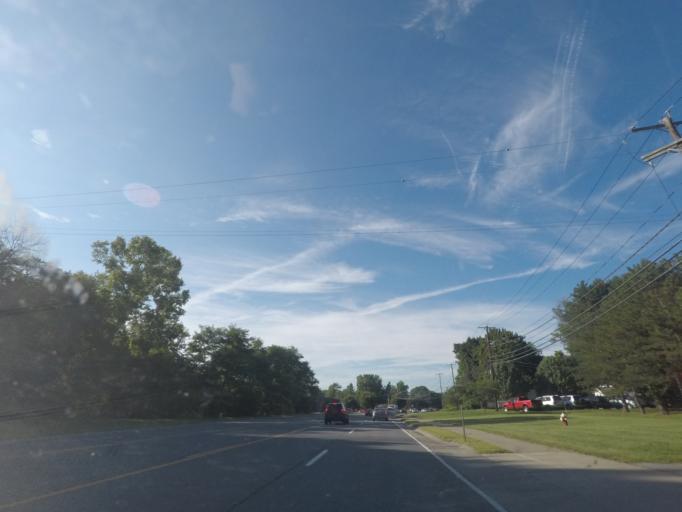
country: US
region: New York
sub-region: Schenectady County
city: Niskayuna
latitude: 42.7634
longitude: -73.8149
